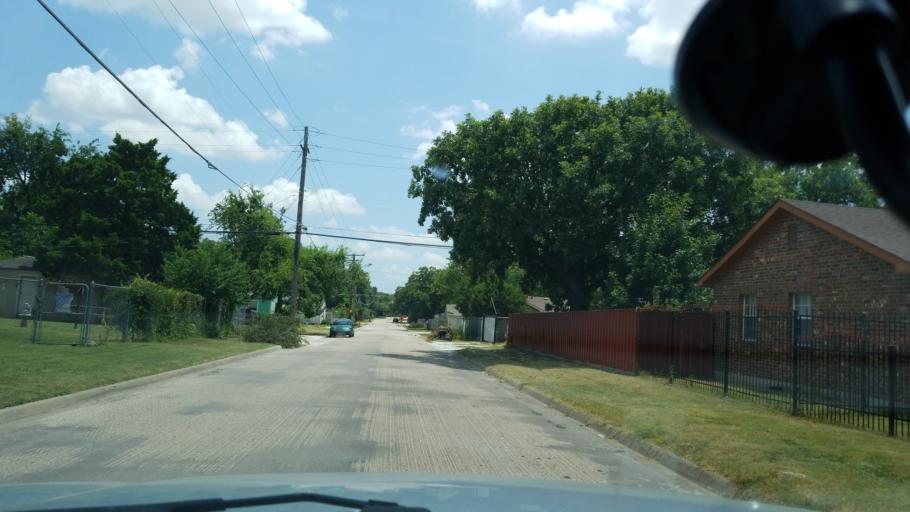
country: US
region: Texas
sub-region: Dallas County
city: Cockrell Hill
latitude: 32.7253
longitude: -96.8721
